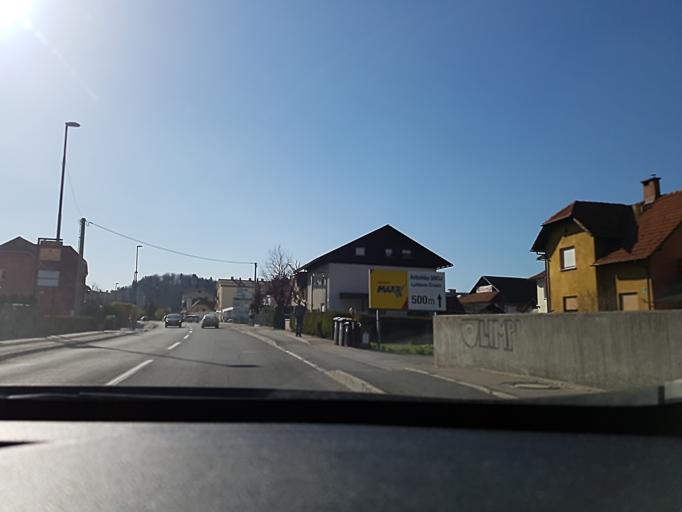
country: SI
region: Trzin
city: Trzin
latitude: 46.1048
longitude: 14.5386
